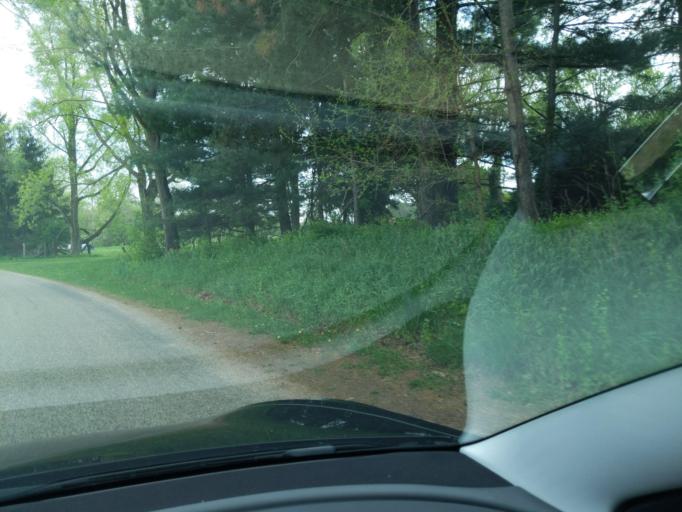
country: US
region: Michigan
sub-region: Ingham County
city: Leslie
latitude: 42.4997
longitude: -84.3390
